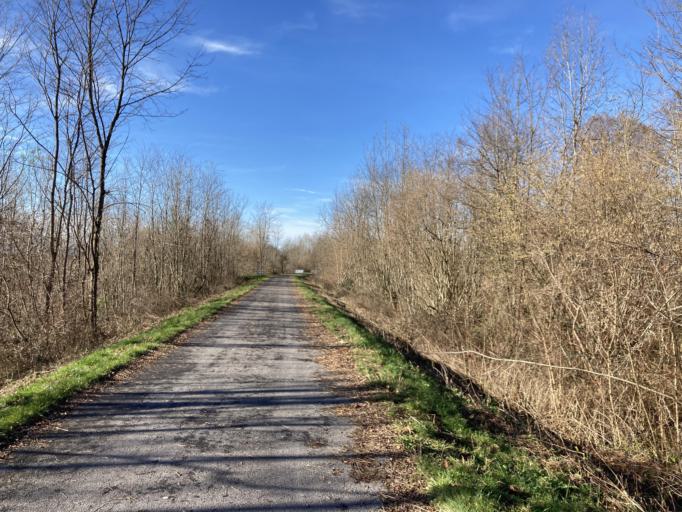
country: FR
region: Aquitaine
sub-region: Departement des Pyrenees-Atlantiques
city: Arudy
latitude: 43.1422
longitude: -0.4536
